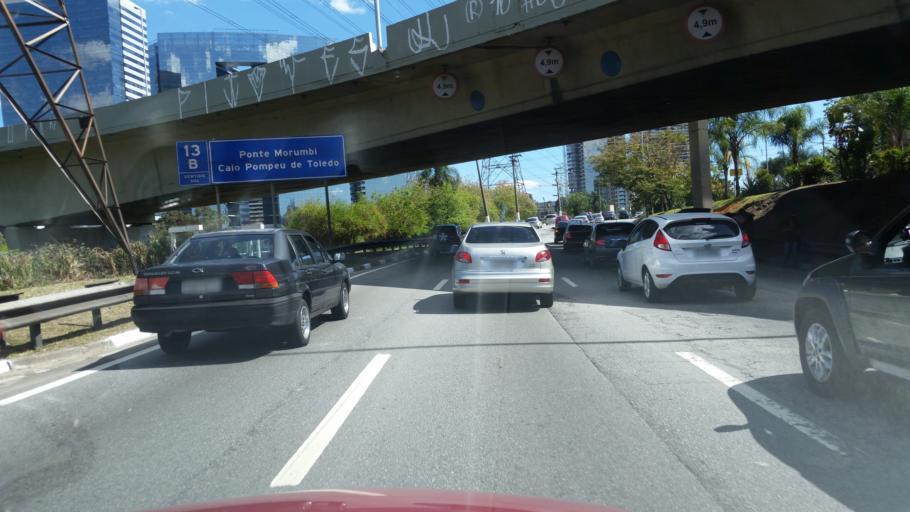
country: BR
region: Sao Paulo
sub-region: Taboao Da Serra
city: Taboao da Serra
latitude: -23.6192
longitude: -46.7019
